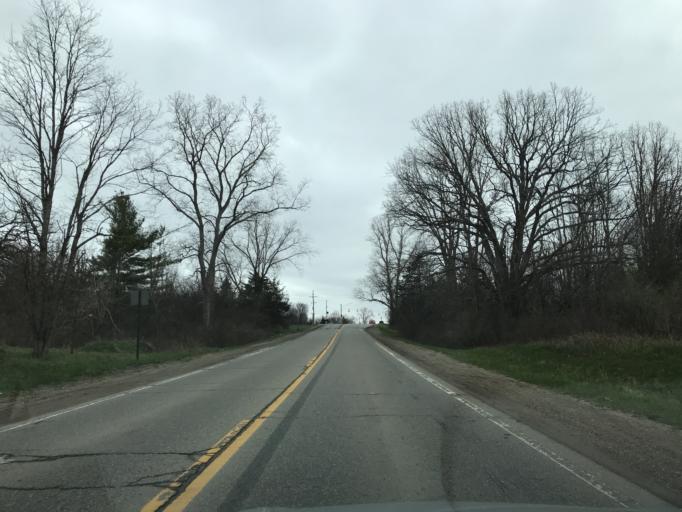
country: US
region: Michigan
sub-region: Oakland County
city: South Lyon
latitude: 42.5152
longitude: -83.6898
